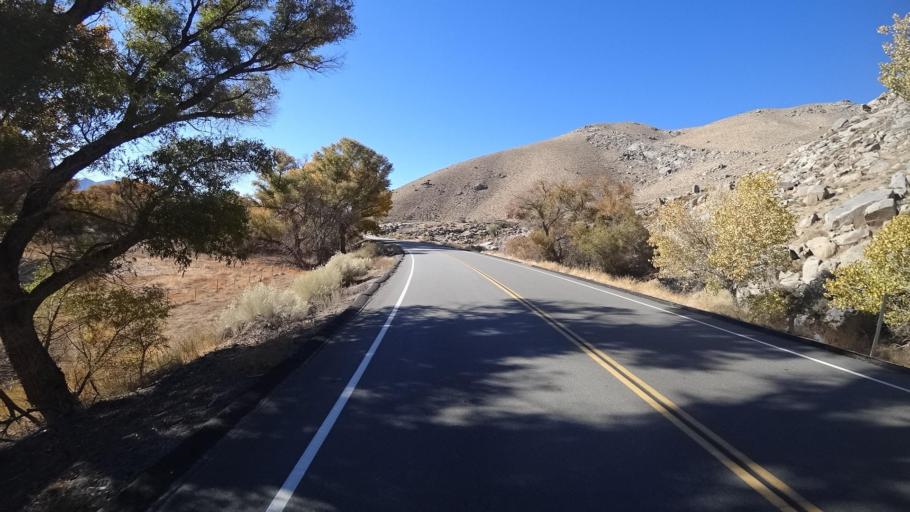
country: US
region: California
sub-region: Kern County
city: Weldon
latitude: 35.6732
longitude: -118.3417
